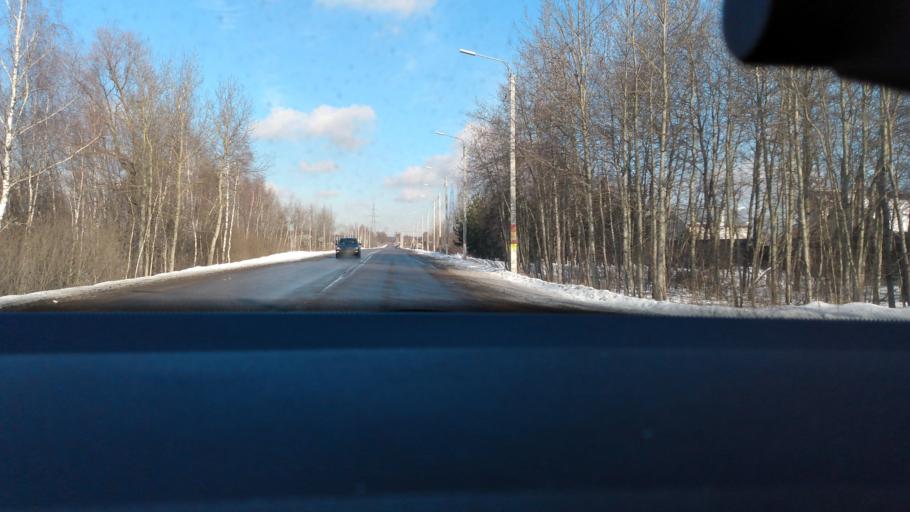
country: RU
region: Moskovskaya
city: Kratovo
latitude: 55.6290
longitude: 38.1601
